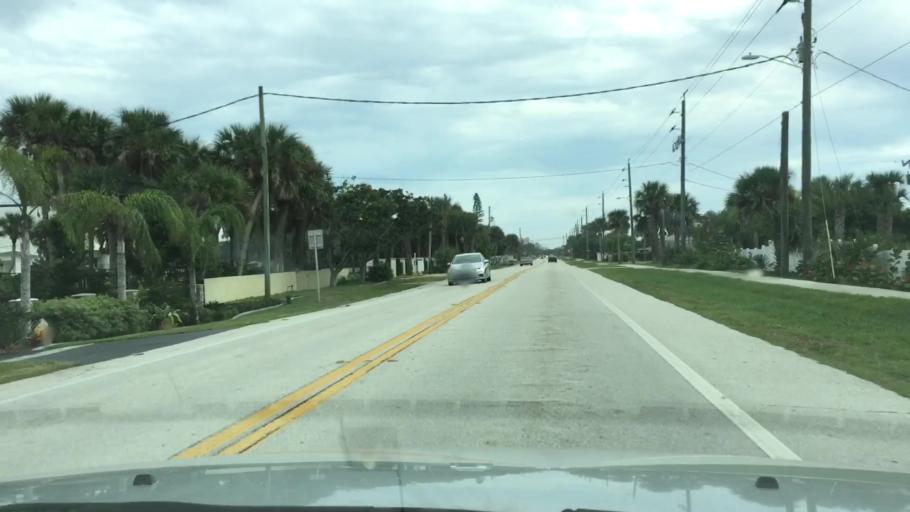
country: US
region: Florida
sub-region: Volusia County
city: Ormond Beach
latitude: 29.3104
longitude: -81.0491
